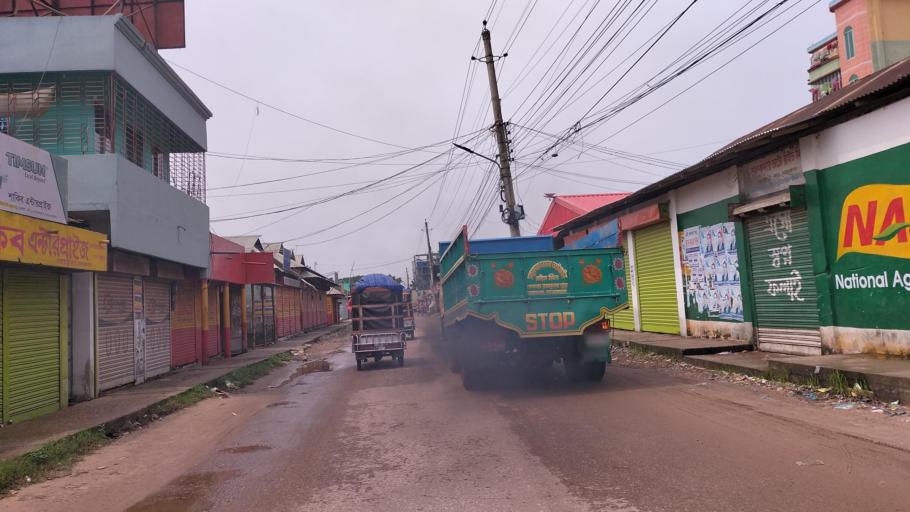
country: BD
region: Dhaka
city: Netrakona
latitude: 24.8897
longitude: 90.7384
